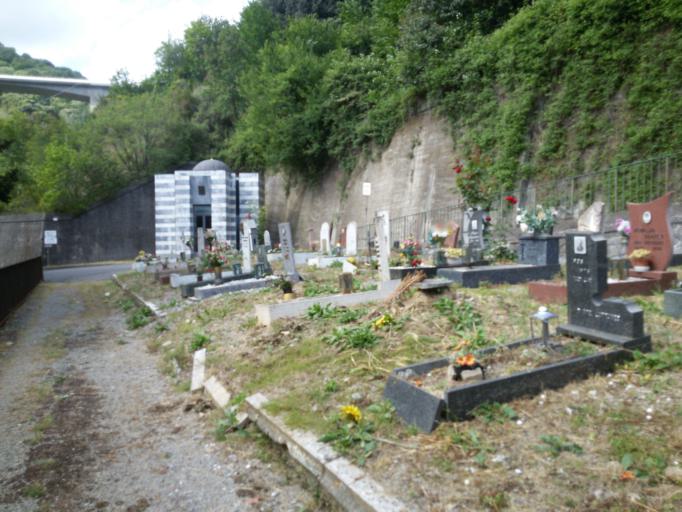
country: IT
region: Liguria
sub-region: Provincia di Genova
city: Genoa
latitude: 44.4349
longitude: 8.9479
